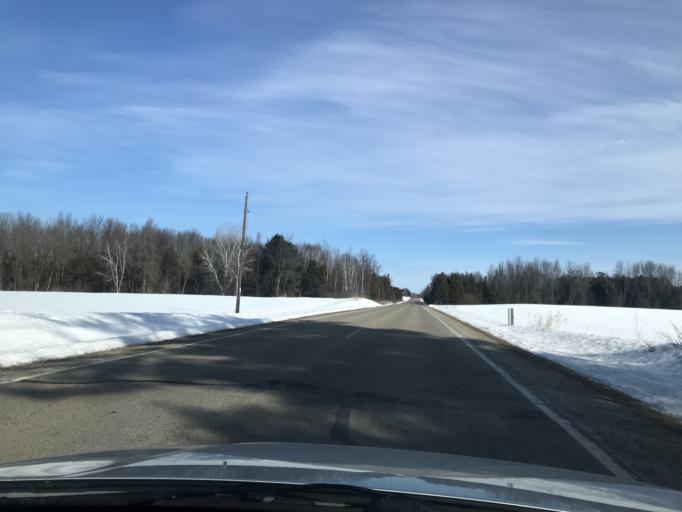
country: US
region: Wisconsin
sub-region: Oconto County
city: Oconto Falls
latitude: 44.9150
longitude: -88.1550
